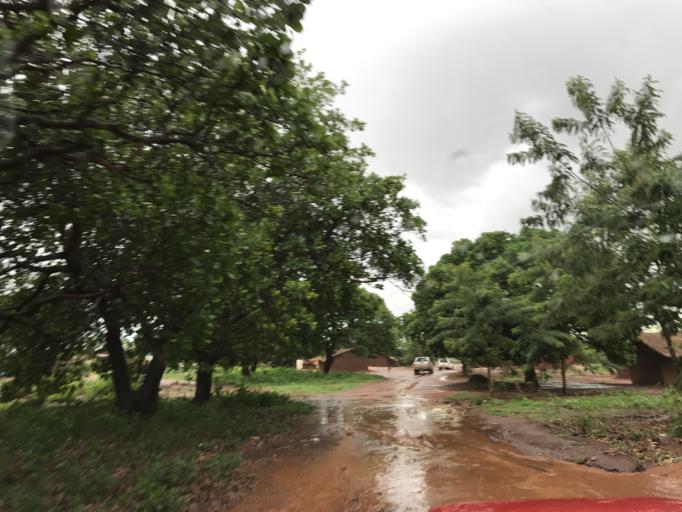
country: MZ
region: Nampula
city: Nacala
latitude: -14.7481
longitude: 39.9860
